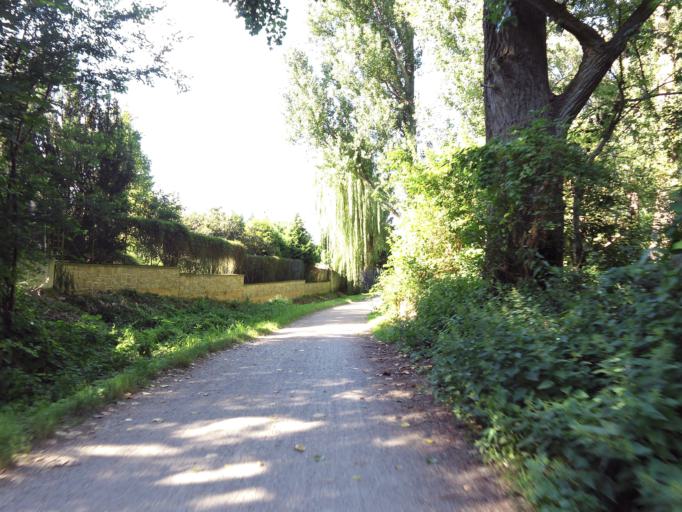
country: DE
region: Rheinland-Pfalz
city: Mutterstadt
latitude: 49.4714
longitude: 8.3648
